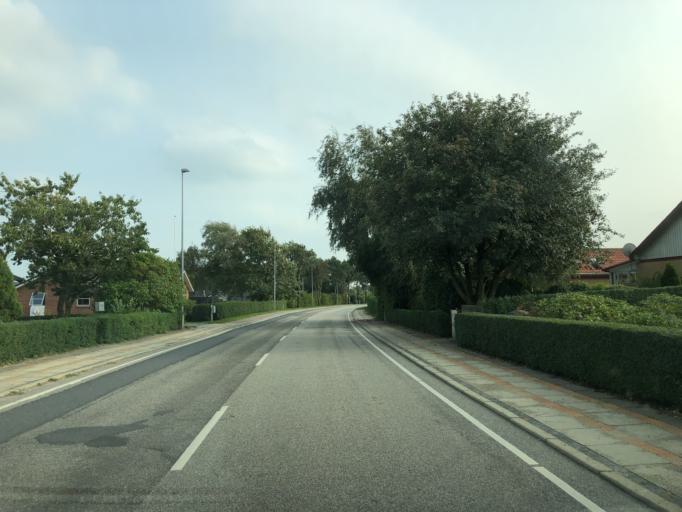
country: DK
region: Central Jutland
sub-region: Ringkobing-Skjern Kommune
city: Videbaek
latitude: 56.0980
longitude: 8.7025
